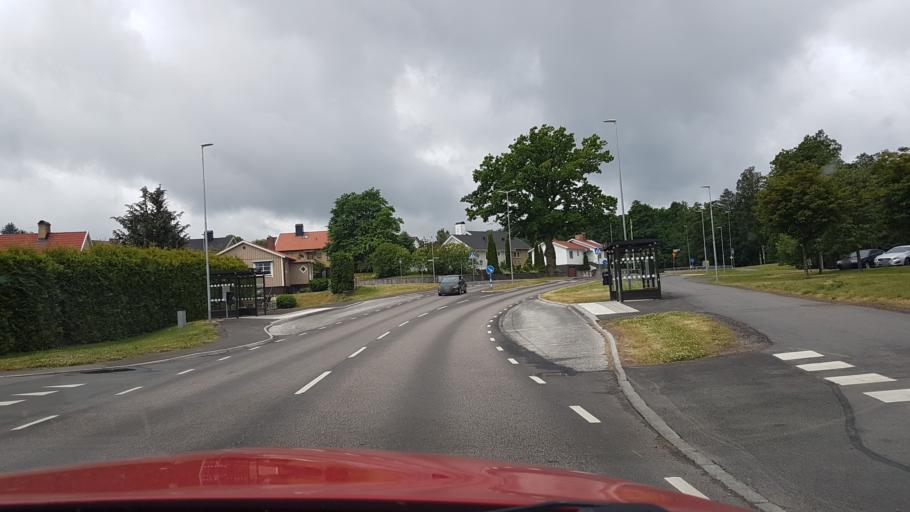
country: SE
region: Vaestra Goetaland
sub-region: Skovde Kommun
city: Skoevde
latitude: 58.3758
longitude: 13.8345
